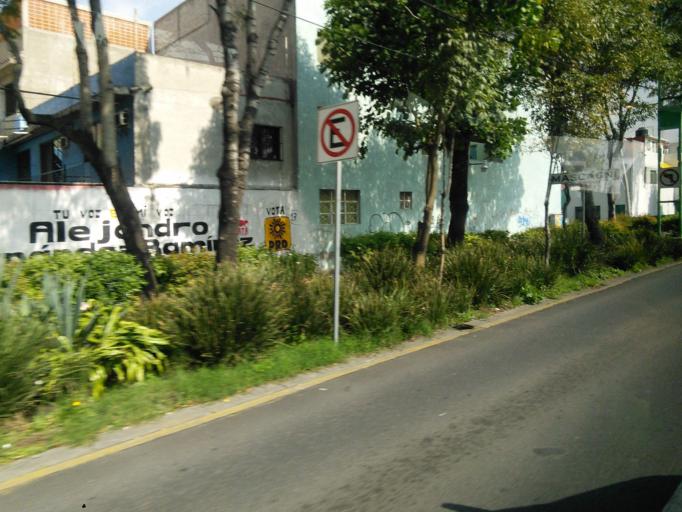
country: MX
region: Mexico City
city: Cuauhtemoc
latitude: 19.4579
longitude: -99.1379
